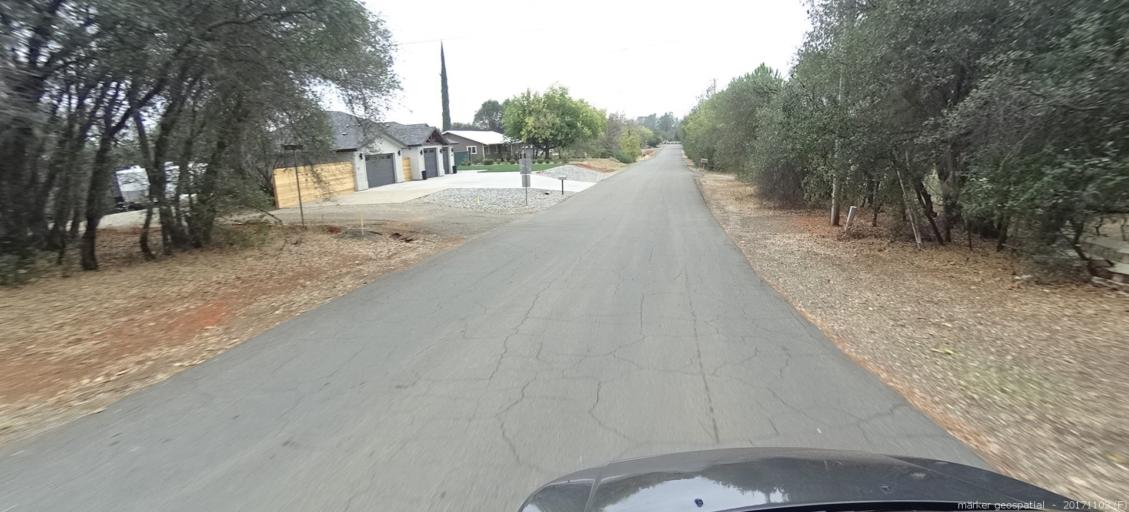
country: US
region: California
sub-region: Shasta County
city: Shasta Lake
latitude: 40.6553
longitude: -122.3100
